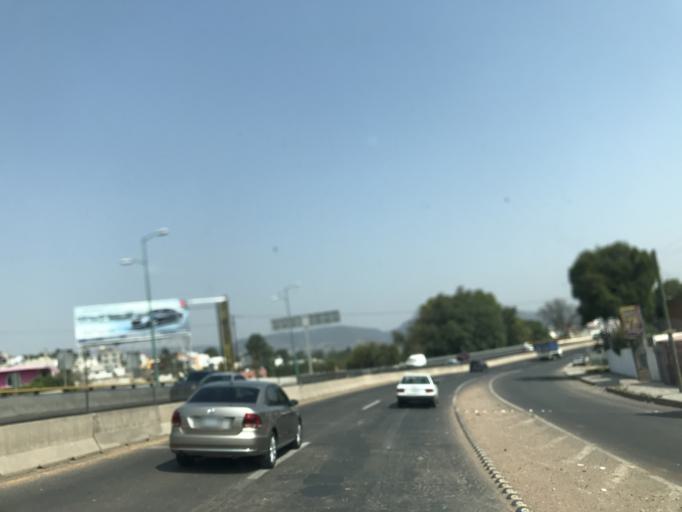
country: MX
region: Tlaxcala
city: Tlaxcala de Xicohtencatl
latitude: 19.3136
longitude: -98.2042
